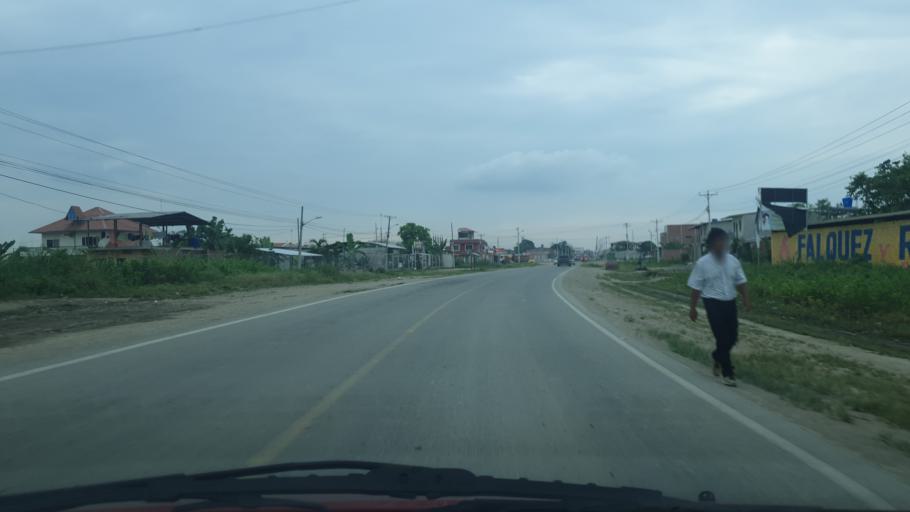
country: EC
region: El Oro
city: Pasaje
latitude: -3.3438
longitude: -79.8145
